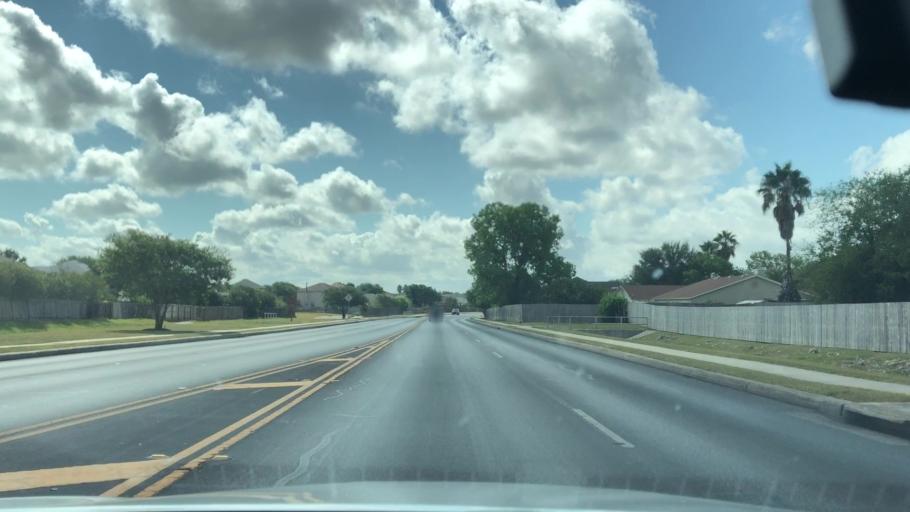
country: US
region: Texas
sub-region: Bexar County
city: Converse
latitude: 29.4957
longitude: -98.3181
